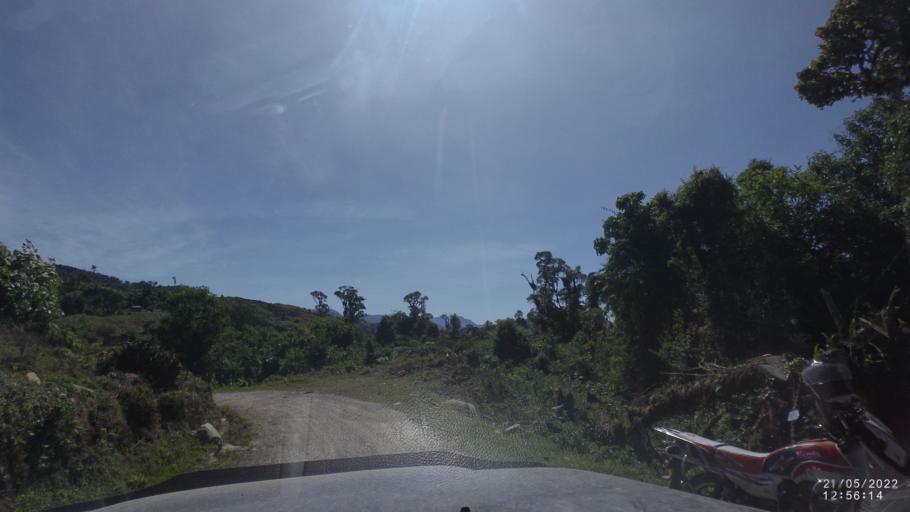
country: BO
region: Cochabamba
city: Colomi
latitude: -17.1735
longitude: -65.9437
